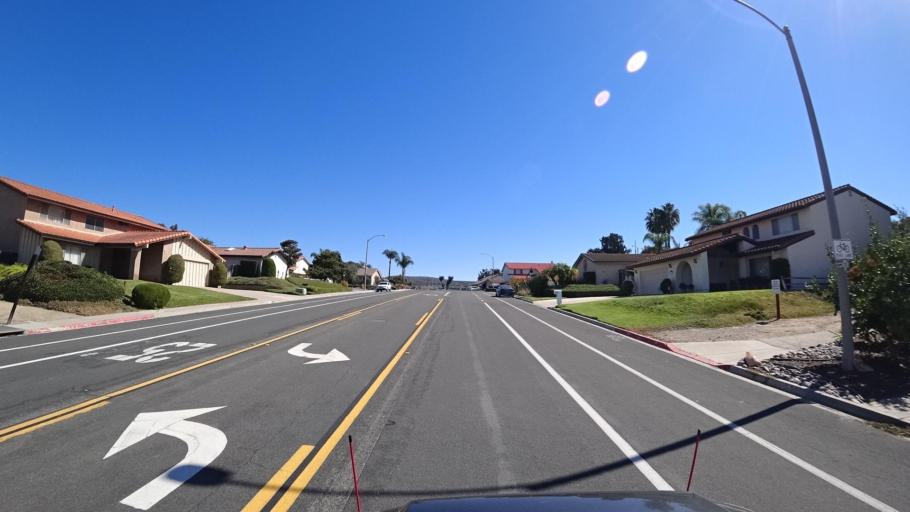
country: US
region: California
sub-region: San Diego County
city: Bonita
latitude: 32.6669
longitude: -117.0004
